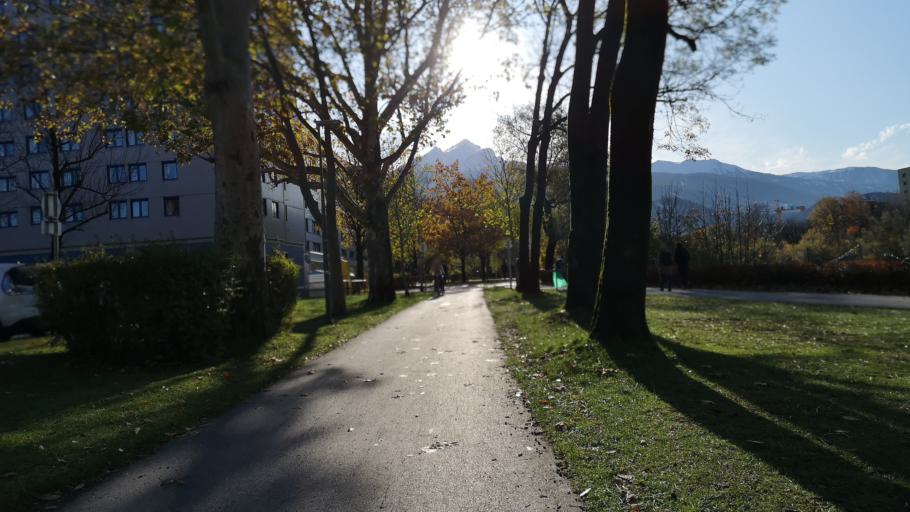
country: AT
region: Tyrol
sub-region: Innsbruck Stadt
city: Innsbruck
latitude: 47.2627
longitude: 11.3827
